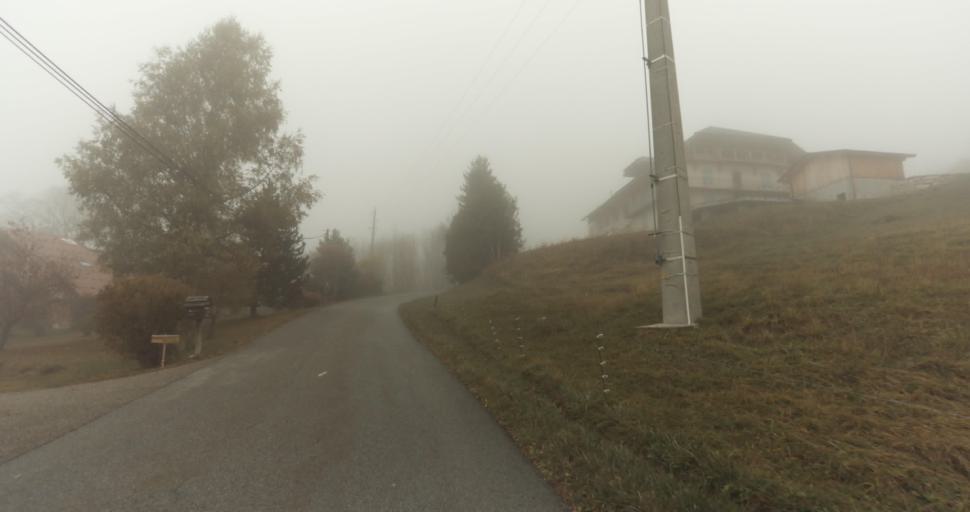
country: FR
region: Rhone-Alpes
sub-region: Departement de la Haute-Savoie
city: Doussard
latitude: 45.8014
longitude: 6.2629
